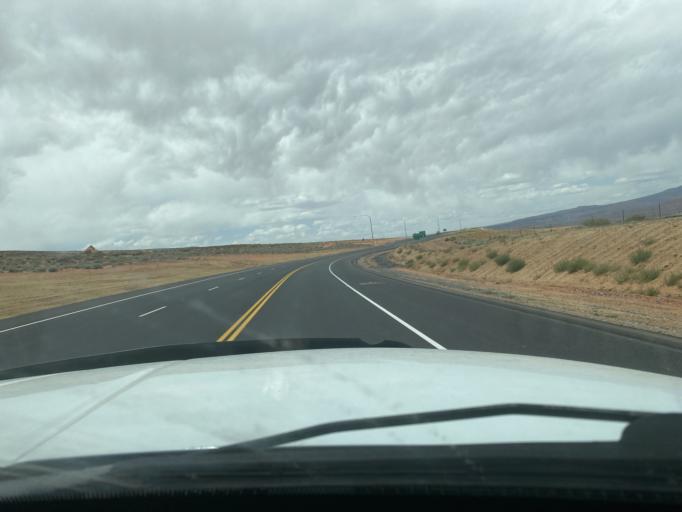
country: US
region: Utah
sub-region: Washington County
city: Washington
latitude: 37.1032
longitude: -113.3909
